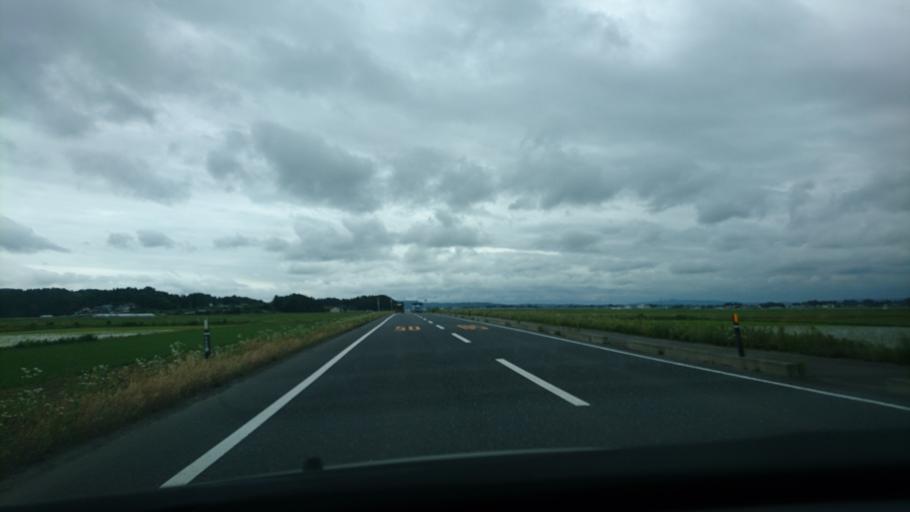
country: JP
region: Miyagi
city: Wakuya
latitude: 38.7044
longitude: 141.2601
